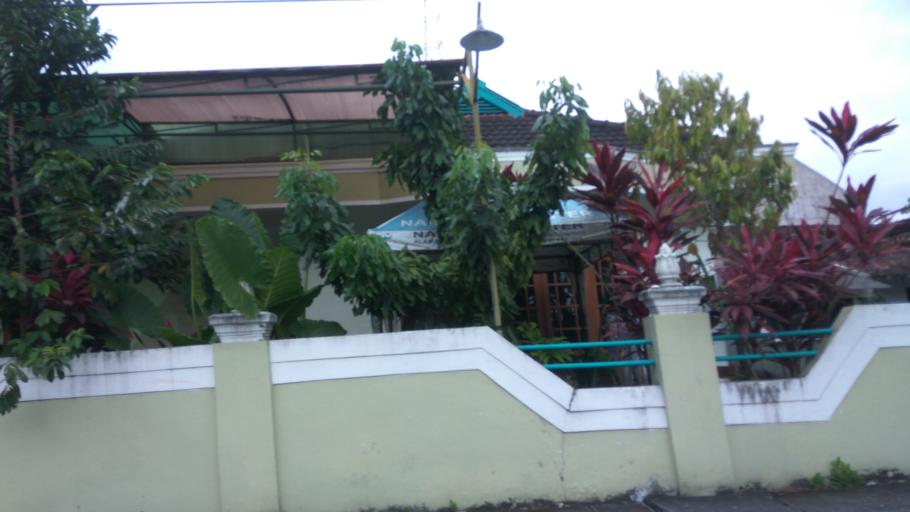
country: ID
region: Daerah Istimewa Yogyakarta
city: Depok
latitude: -7.7356
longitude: 110.4060
